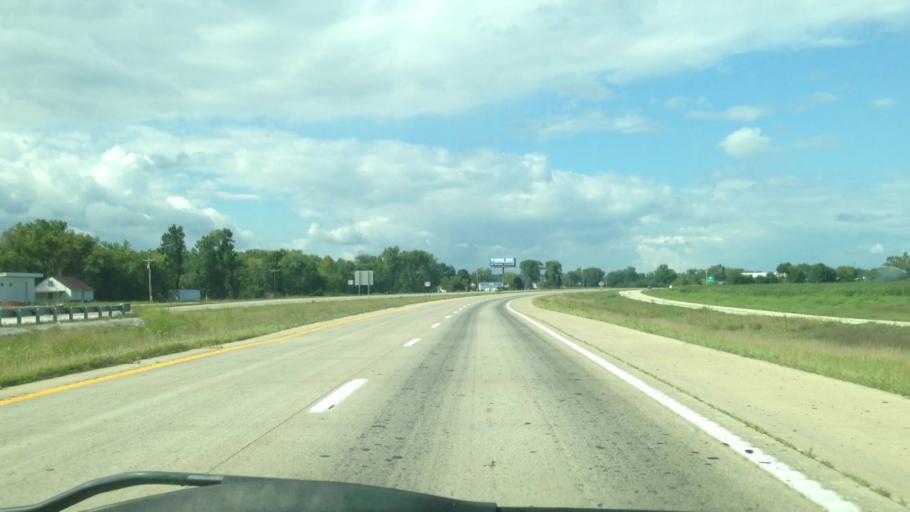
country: US
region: Missouri
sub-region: Clark County
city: Kahoka
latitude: 40.3722
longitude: -91.5880
